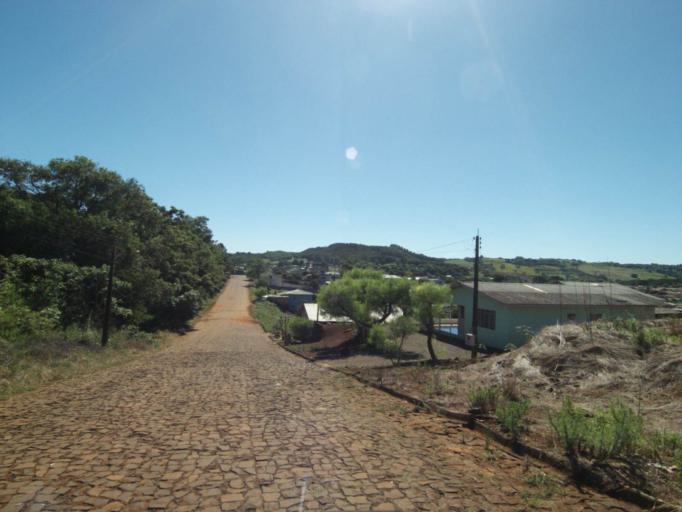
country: BR
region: Santa Catarina
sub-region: Sao Lourenco Do Oeste
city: Sao Lourenco dOeste
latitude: -26.2693
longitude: -52.7842
